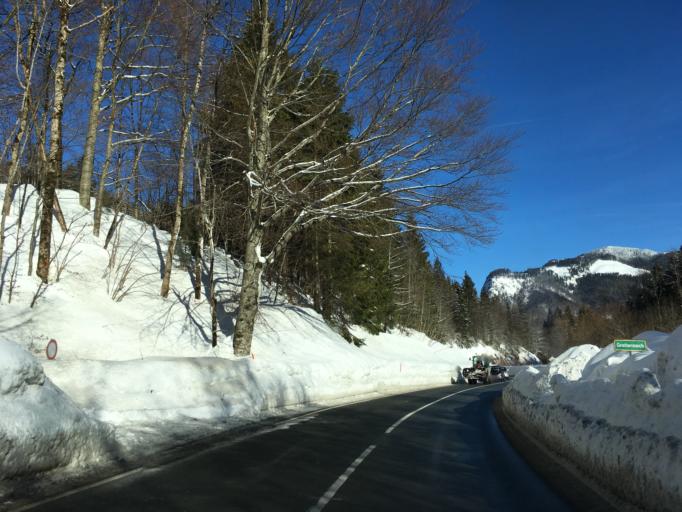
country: AT
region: Tyrol
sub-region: Politischer Bezirk Kufstein
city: Rettenschoss
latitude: 47.7197
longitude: 12.2894
